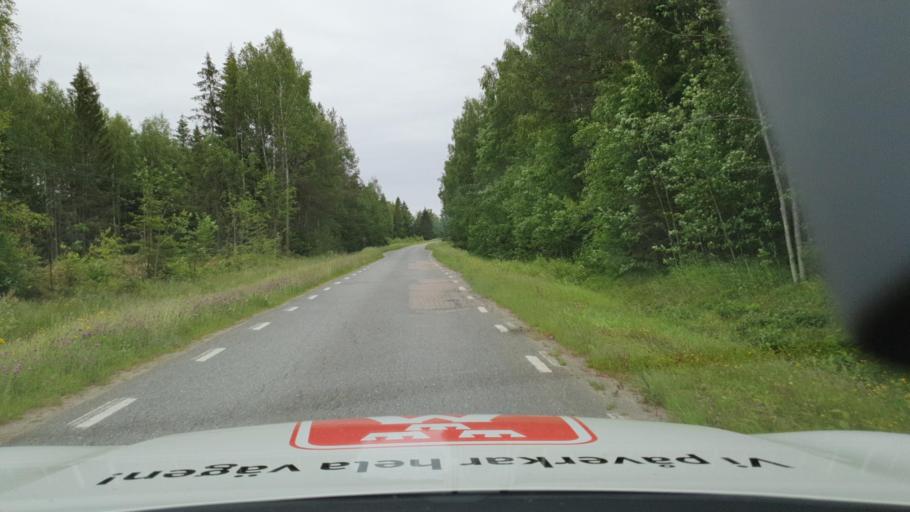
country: SE
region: Vaesterbotten
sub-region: Nordmalings Kommun
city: Nordmaling
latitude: 63.4727
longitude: 19.4618
